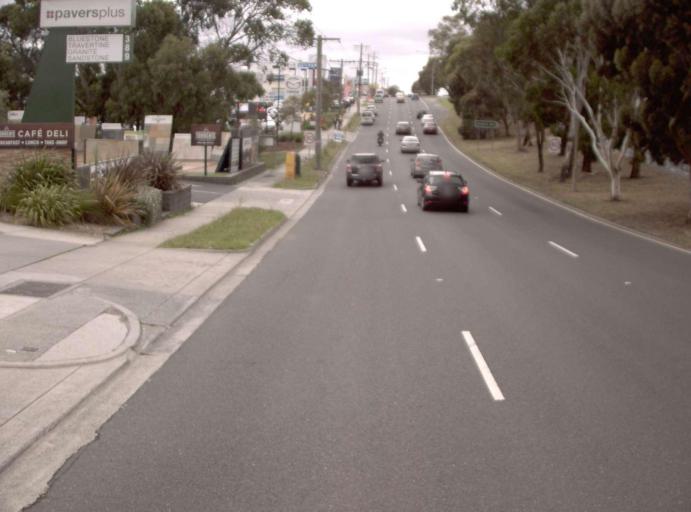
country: AU
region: Victoria
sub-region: Maroondah
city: Ringwood East
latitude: -37.8044
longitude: 145.2455
